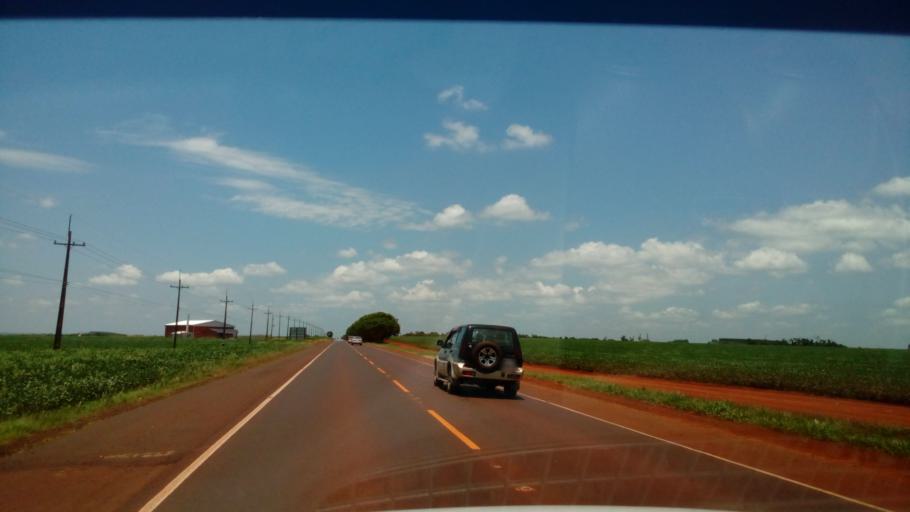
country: PY
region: Alto Parana
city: Naranjal
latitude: -25.9393
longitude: -55.1190
